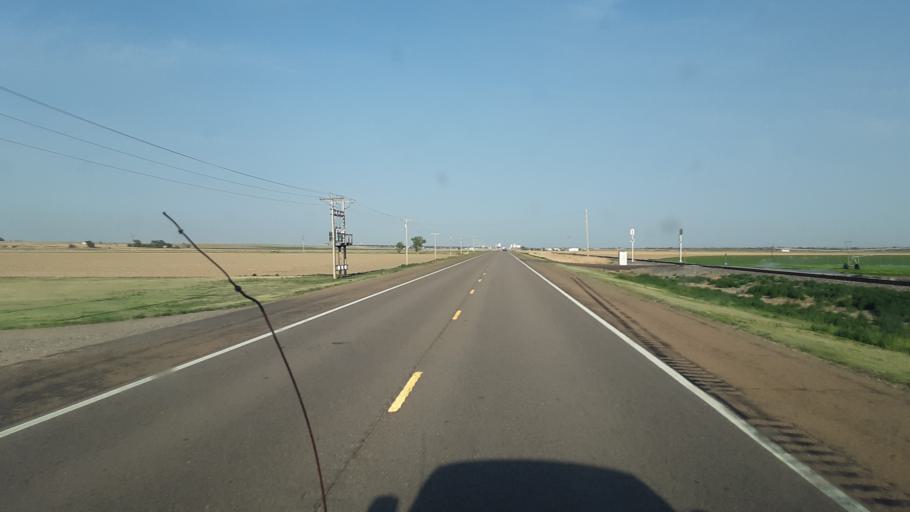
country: US
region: Kansas
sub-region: Hamilton County
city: Syracuse
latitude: 37.9980
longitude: -101.8217
